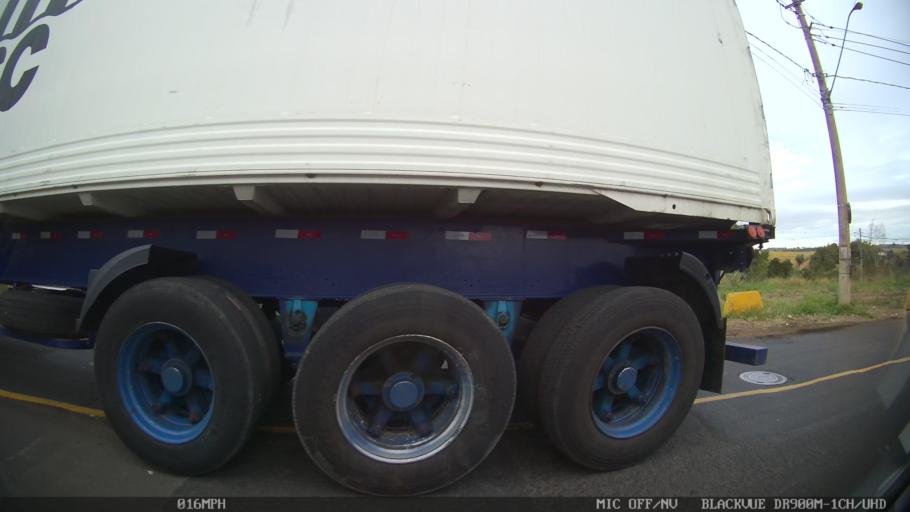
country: BR
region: Sao Paulo
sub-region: Sao Jose Do Rio Preto
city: Sao Jose do Rio Preto
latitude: -20.8304
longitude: -49.4255
